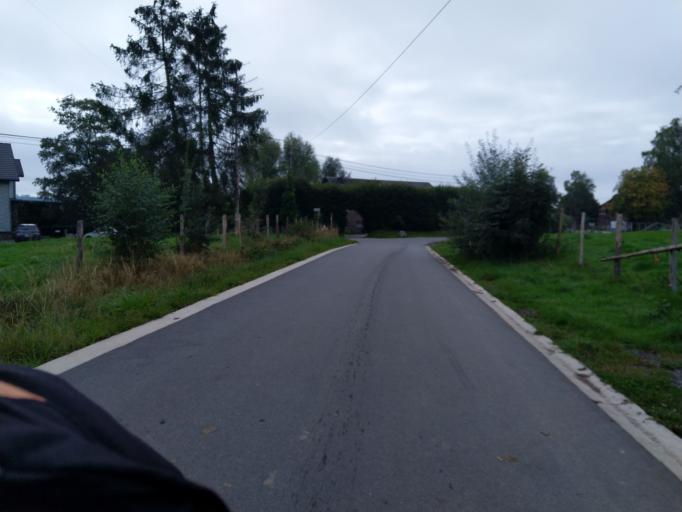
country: BE
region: Wallonia
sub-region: Province de Liege
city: Malmedy
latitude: 50.4579
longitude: 6.0525
